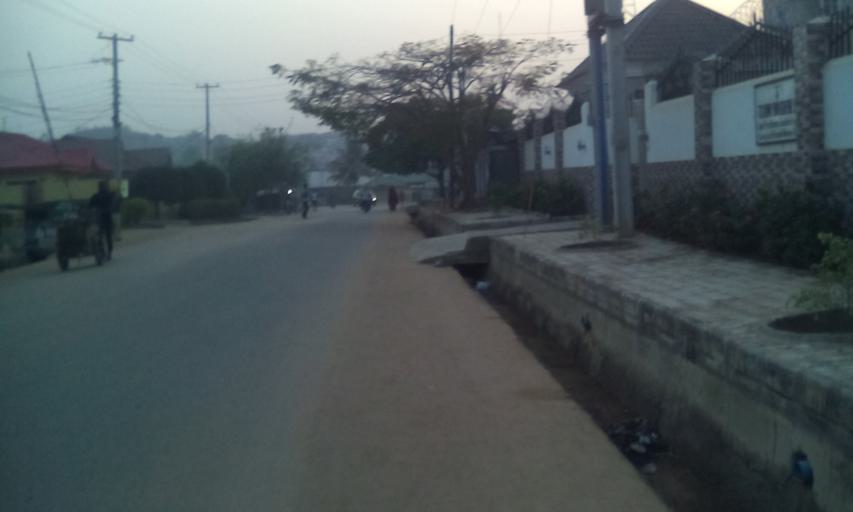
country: NG
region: Abuja Federal Capital Territory
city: Abuja
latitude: 8.9835
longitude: 7.3592
